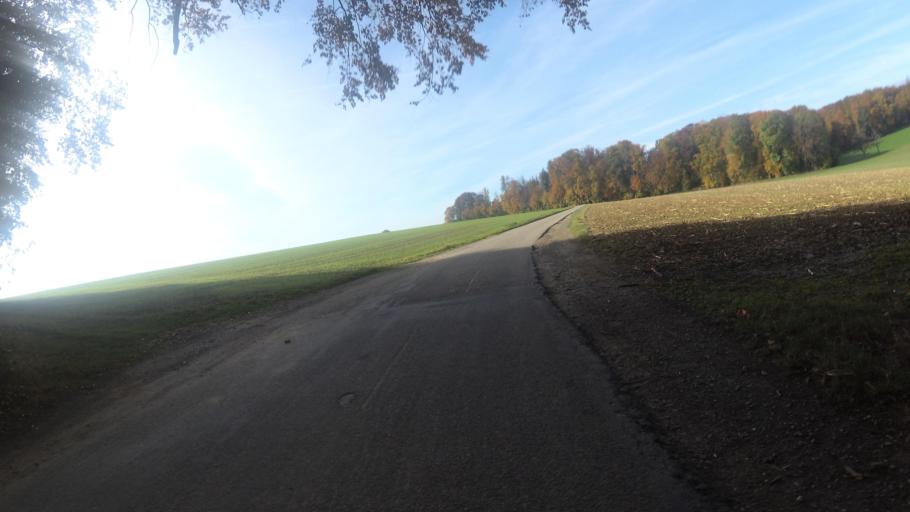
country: DE
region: Baden-Wuerttemberg
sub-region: Karlsruhe Region
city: Billigheim
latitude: 49.3100
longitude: 9.2202
